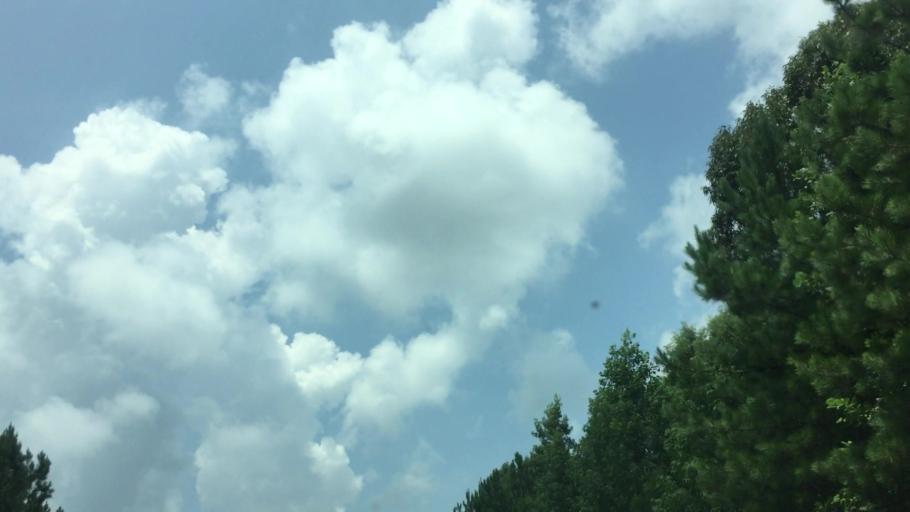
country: US
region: Georgia
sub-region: Fulton County
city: Chattahoochee Hills
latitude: 33.5646
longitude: -84.7786
